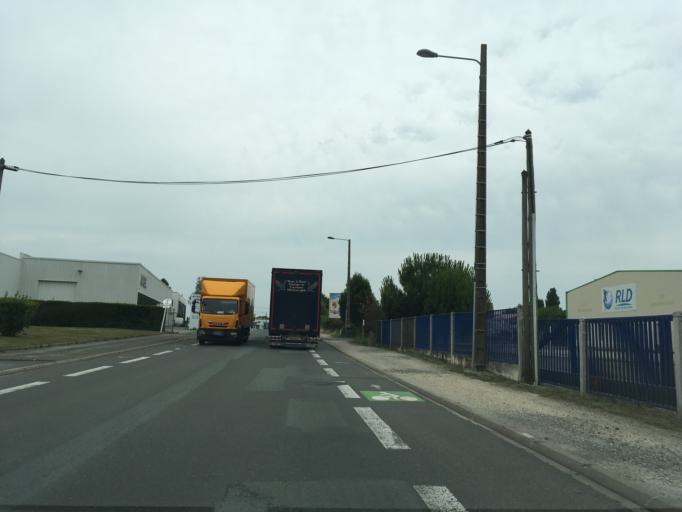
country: FR
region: Poitou-Charentes
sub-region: Departement des Deux-Sevres
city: Bessines
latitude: 46.3119
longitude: -0.4956
